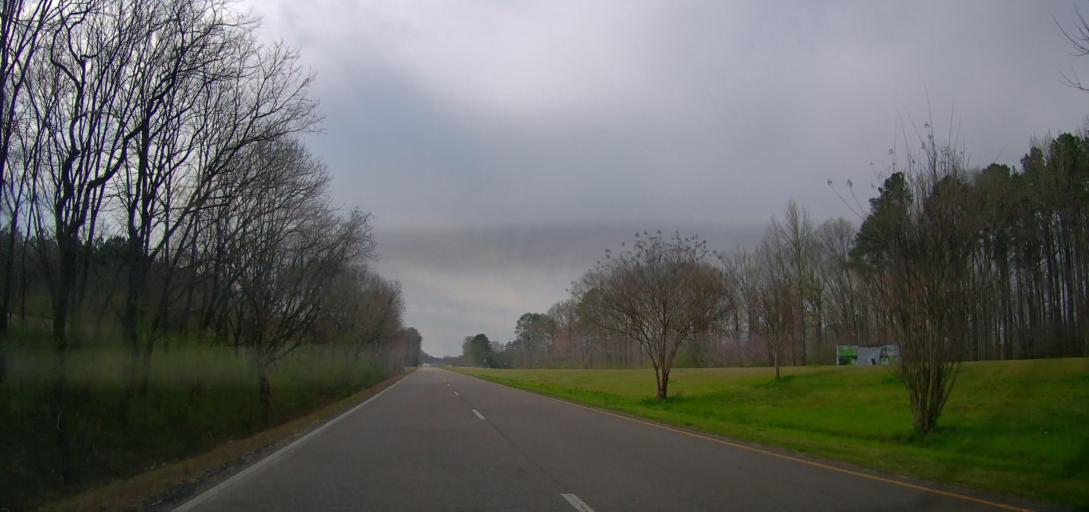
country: US
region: Alabama
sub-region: Walker County
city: Carbon Hill
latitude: 33.8792
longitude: -87.5028
